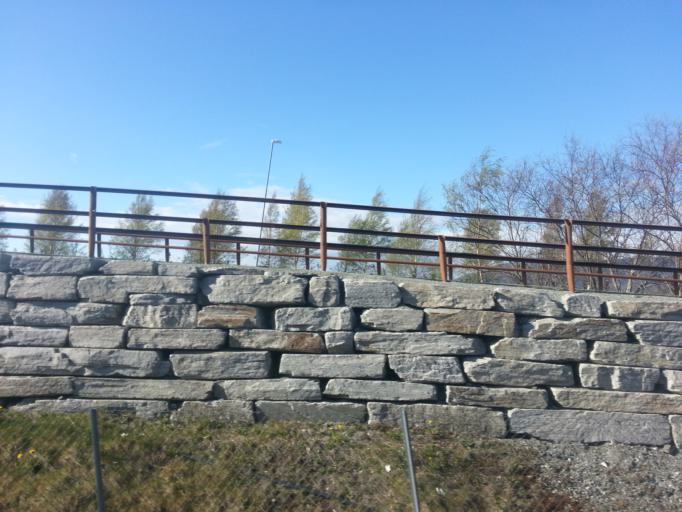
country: NO
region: Nord-Trondelag
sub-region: Stjordal
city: Stjordal
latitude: 63.4456
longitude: 10.8881
